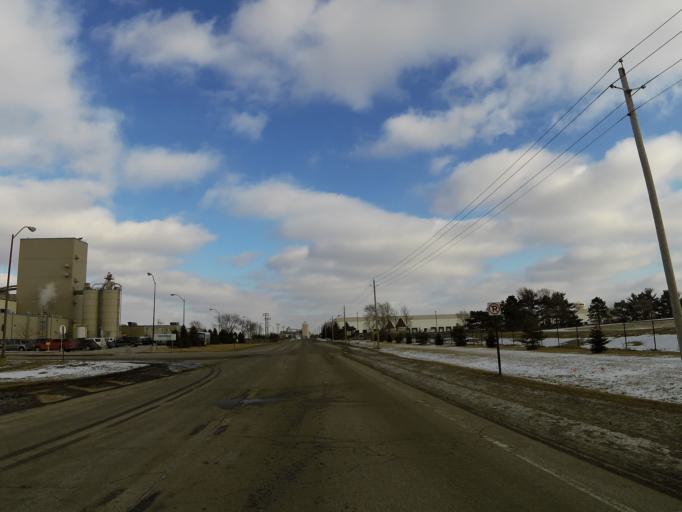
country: US
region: Minnesota
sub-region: Scott County
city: Shakopee
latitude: 44.7974
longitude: -93.4824
